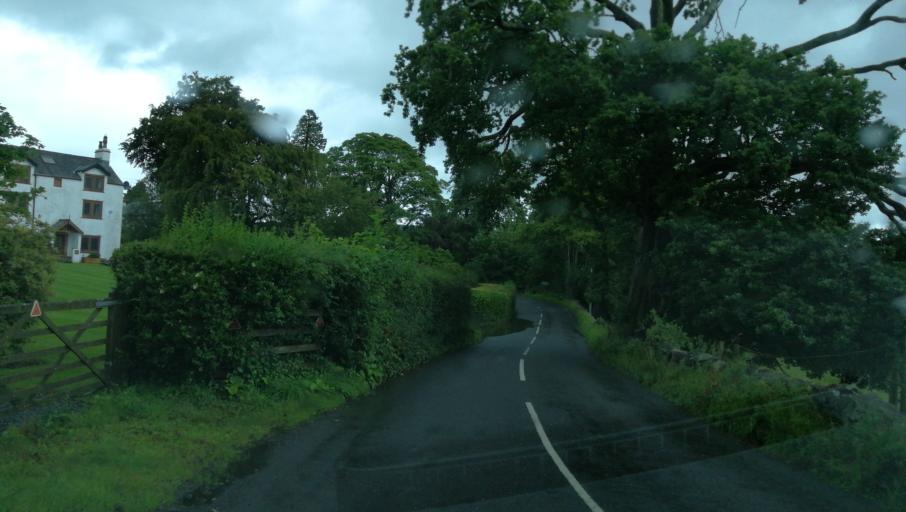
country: GB
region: England
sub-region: Cumbria
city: Penrith
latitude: 54.5932
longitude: -2.8592
